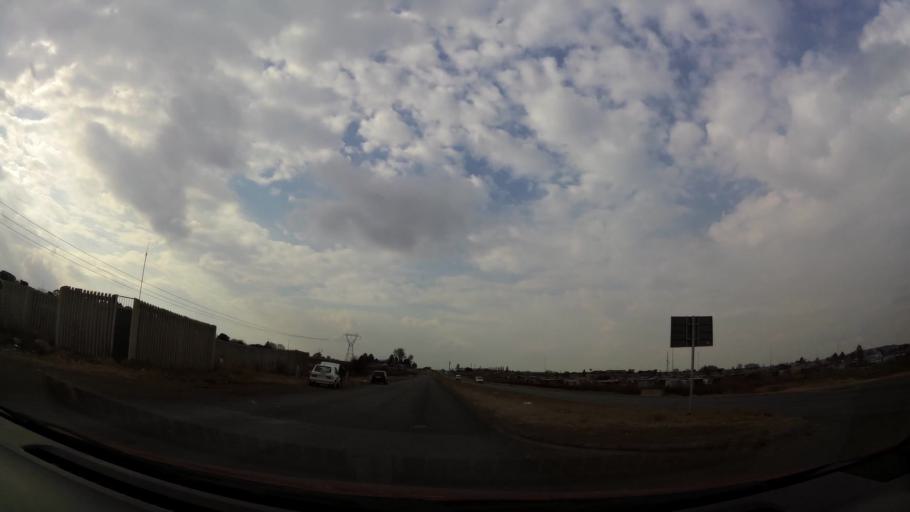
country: ZA
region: Gauteng
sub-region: Sedibeng District Municipality
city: Vanderbijlpark
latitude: -26.6662
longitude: 27.8402
